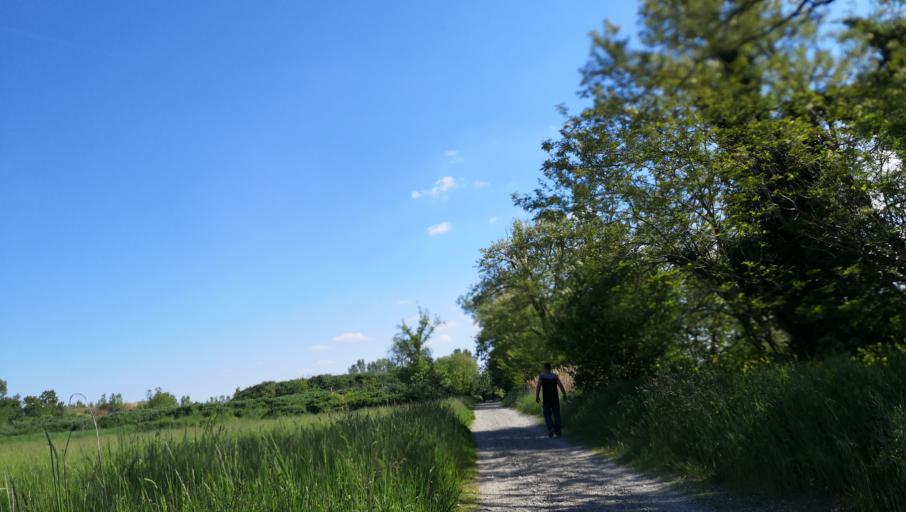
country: FR
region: Midi-Pyrenees
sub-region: Departement de la Haute-Garonne
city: Aucamville
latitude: 43.6591
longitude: 1.4073
